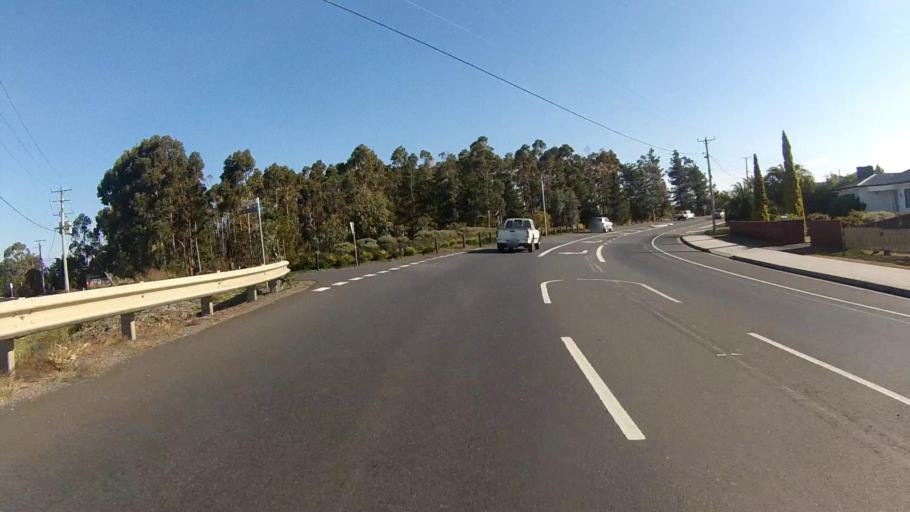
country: AU
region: Tasmania
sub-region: Sorell
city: Sorell
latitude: -42.7904
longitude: 147.5615
